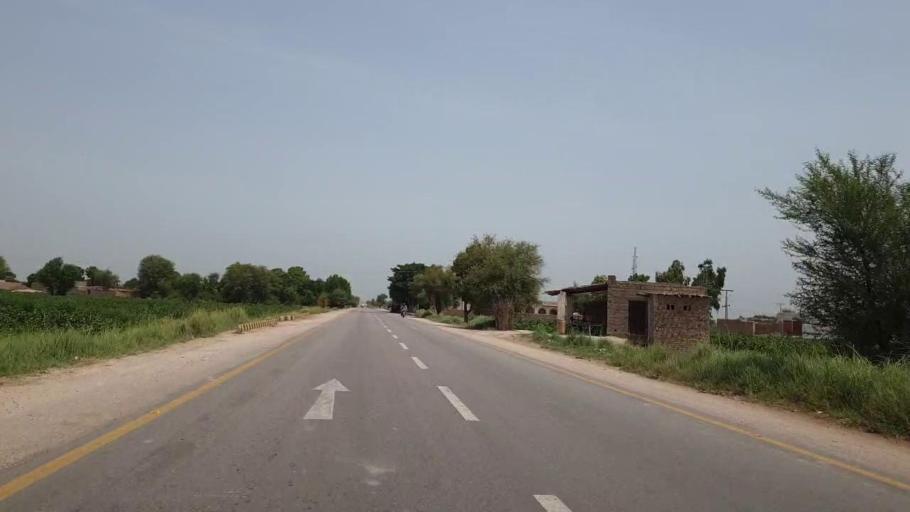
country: PK
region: Sindh
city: Shahpur Chakar
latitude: 26.1558
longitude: 68.6334
